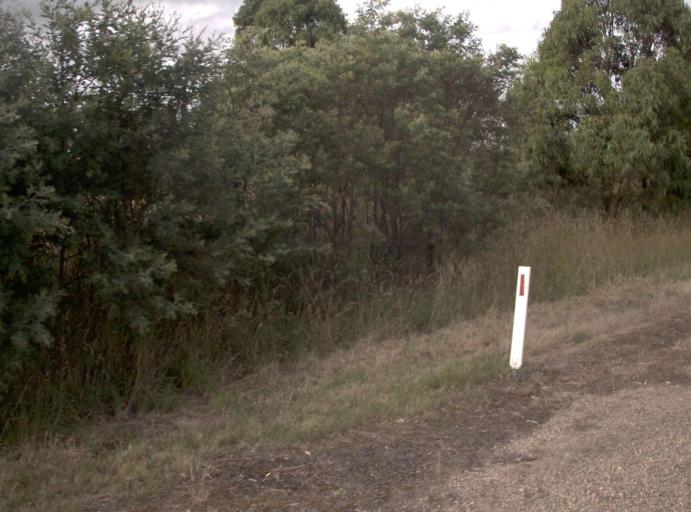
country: AU
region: Victoria
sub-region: Wellington
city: Sale
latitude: -37.8526
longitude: 147.0461
